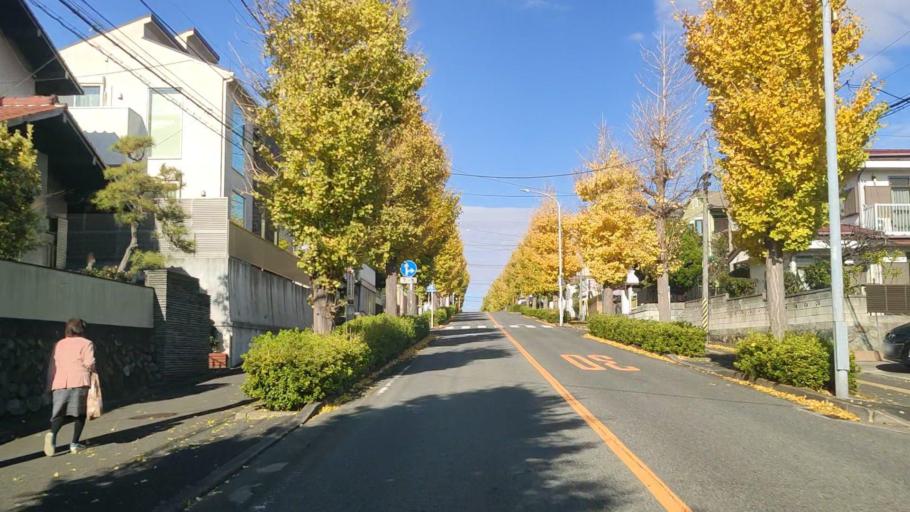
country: JP
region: Kanagawa
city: Minami-rinkan
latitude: 35.4549
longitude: 139.5350
